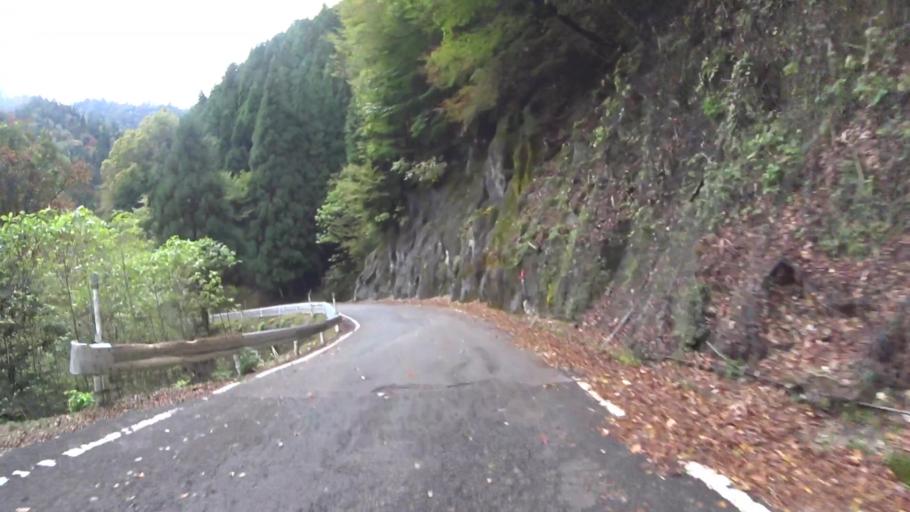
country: JP
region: Fukui
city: Obama
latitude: 35.2771
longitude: 135.7185
